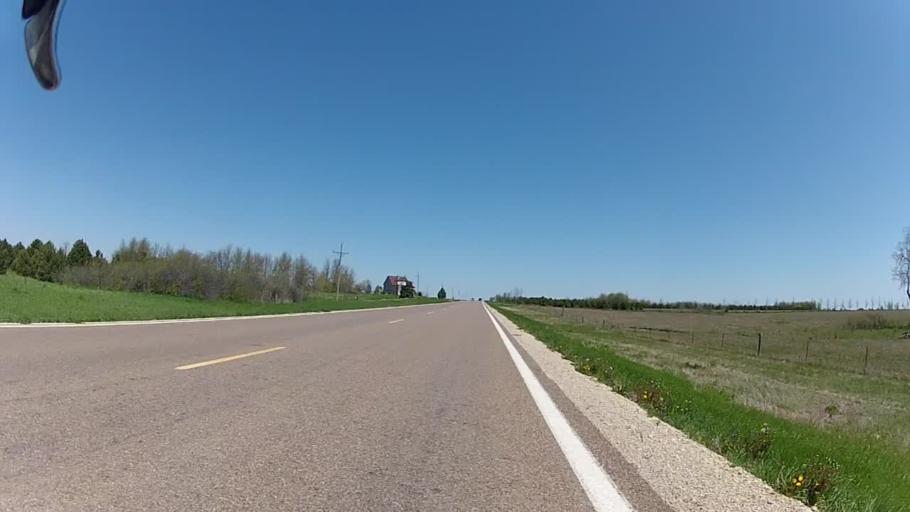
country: US
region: Kansas
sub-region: Riley County
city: Manhattan
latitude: 38.9554
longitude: -96.5202
